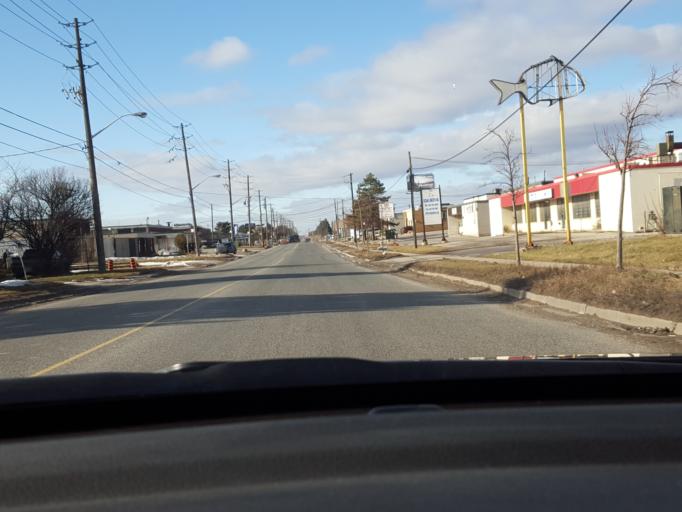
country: CA
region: Ontario
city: Concord
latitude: 43.7583
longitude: -79.5459
